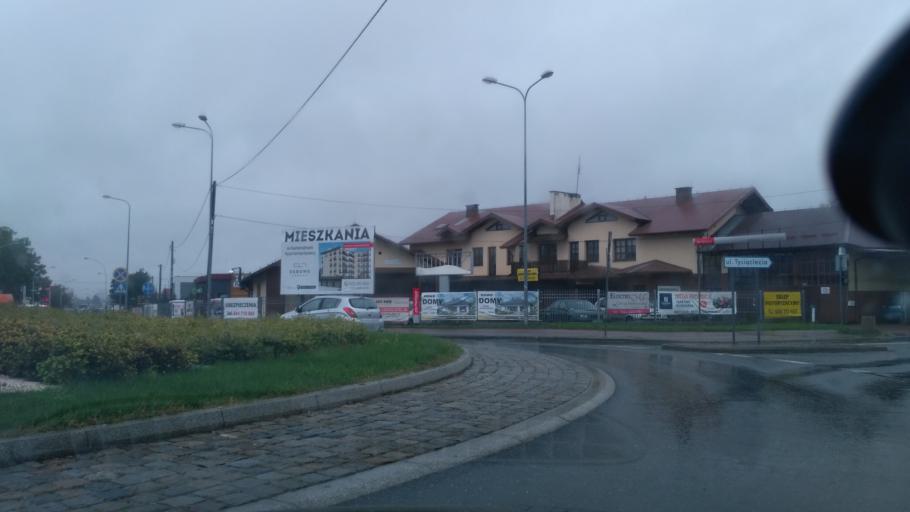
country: PL
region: Subcarpathian Voivodeship
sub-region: Powiat debicki
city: Debica
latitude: 50.0544
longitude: 21.4313
